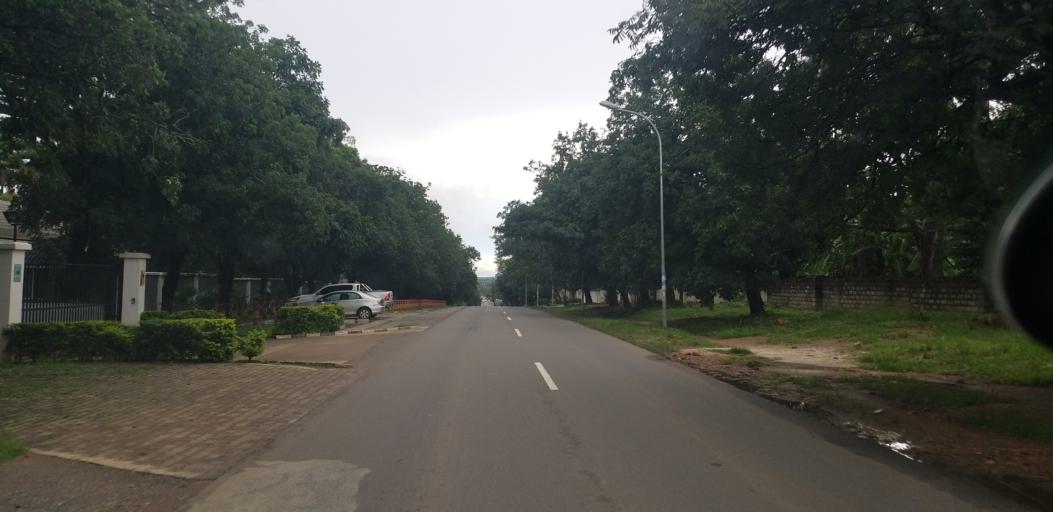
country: ZM
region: Lusaka
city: Lusaka
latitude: -15.4327
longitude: 28.3480
